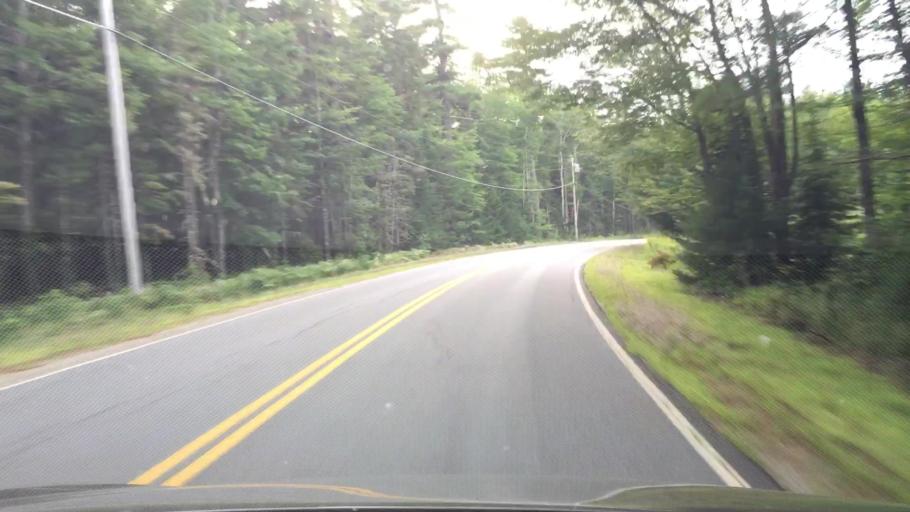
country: US
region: Maine
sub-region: Hancock County
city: Penobscot
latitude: 44.4503
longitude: -68.6938
